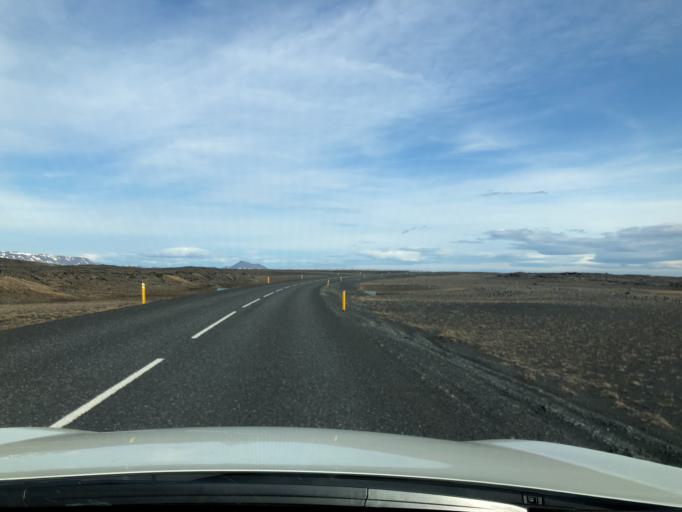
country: IS
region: Northeast
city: Laugar
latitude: 65.6899
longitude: -16.3880
